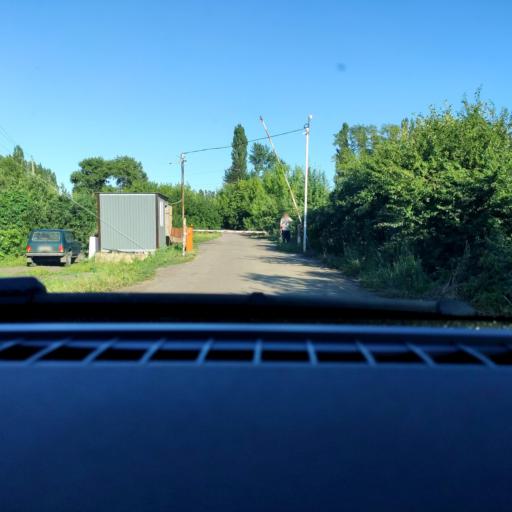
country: RU
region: Voronezj
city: Maslovka
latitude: 51.5158
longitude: 39.2202
